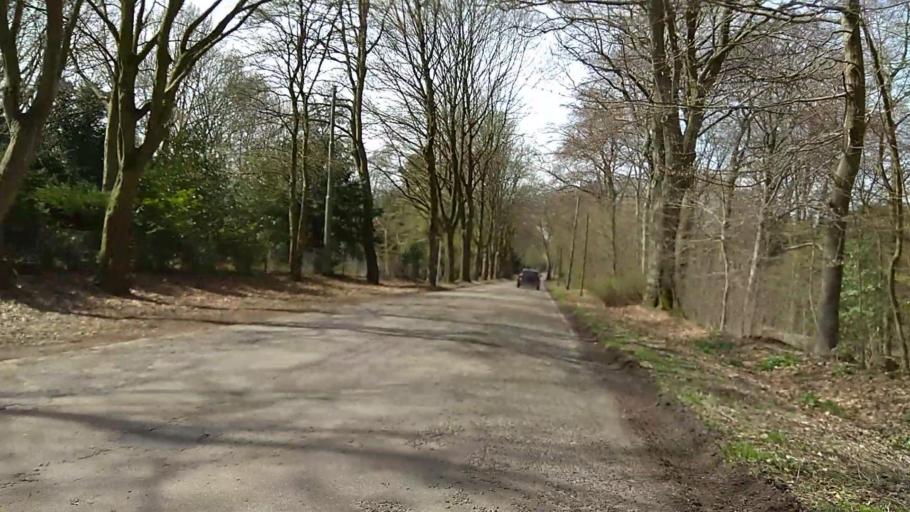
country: DE
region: North Rhine-Westphalia
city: Herten
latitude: 51.5772
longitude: 7.0838
